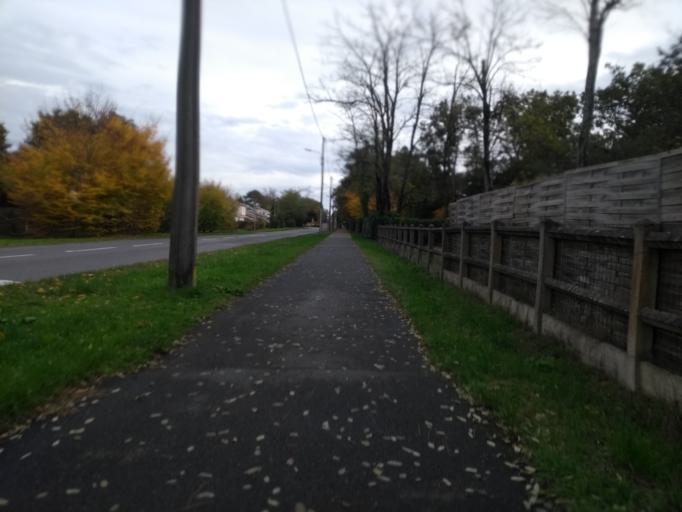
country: FR
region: Aquitaine
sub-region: Departement de la Gironde
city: Cestas
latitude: 44.7375
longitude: -0.6751
